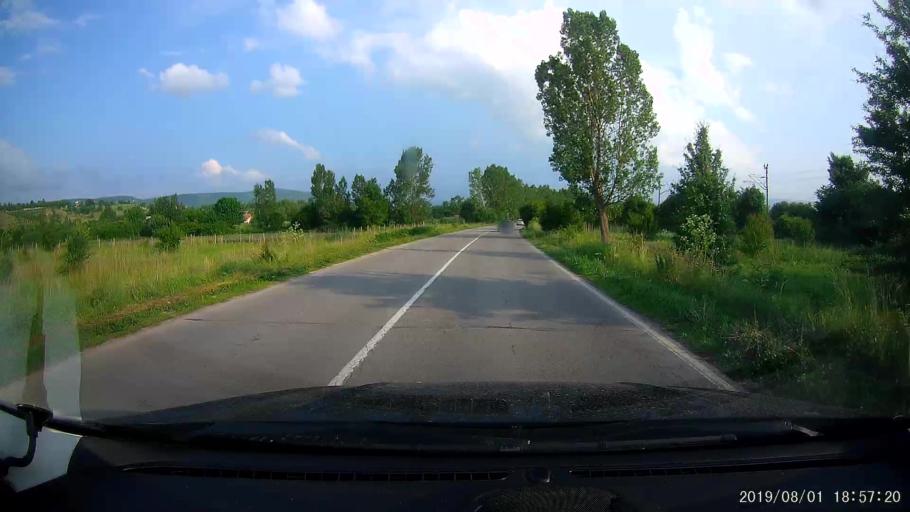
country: BG
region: Shumen
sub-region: Obshtina Smyadovo
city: Smyadovo
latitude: 43.1487
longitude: 27.0226
